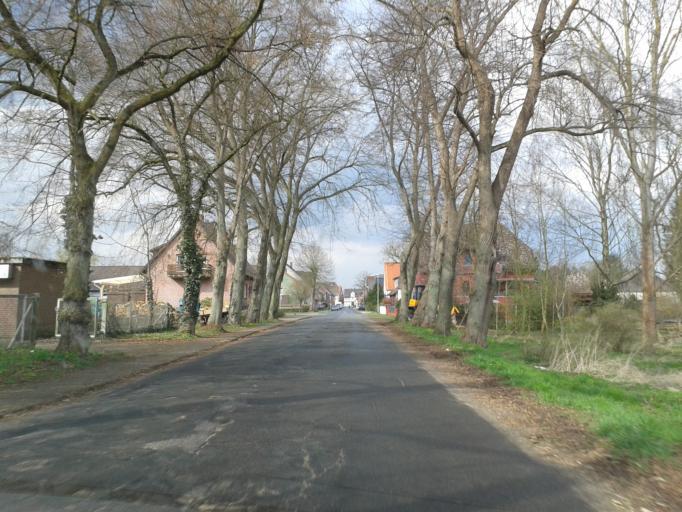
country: DE
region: Lower Saxony
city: Bergen an der Dumme
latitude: 52.8871
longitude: 10.9621
